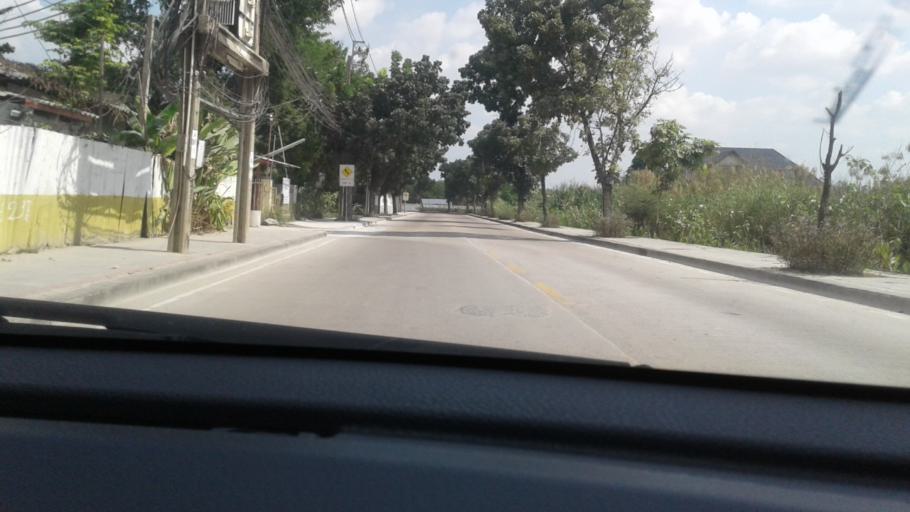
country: TH
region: Bangkok
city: Taling Chan
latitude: 13.7881
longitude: 100.4021
